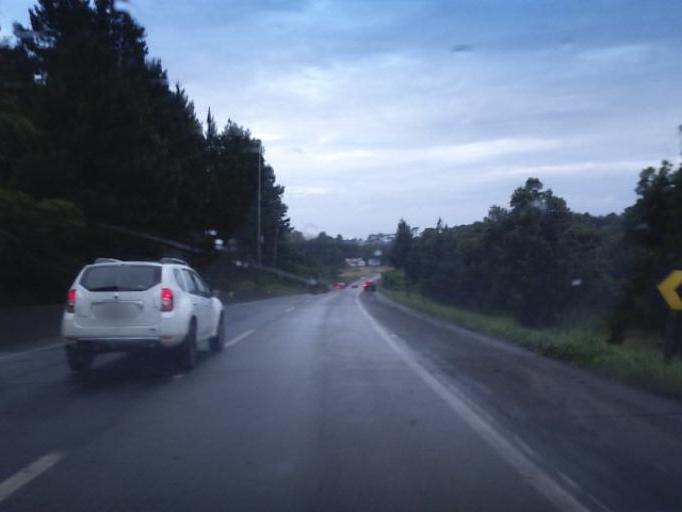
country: BR
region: Parana
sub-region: Sao Jose Dos Pinhais
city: Sao Jose dos Pinhais
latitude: -25.8516
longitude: -49.0199
